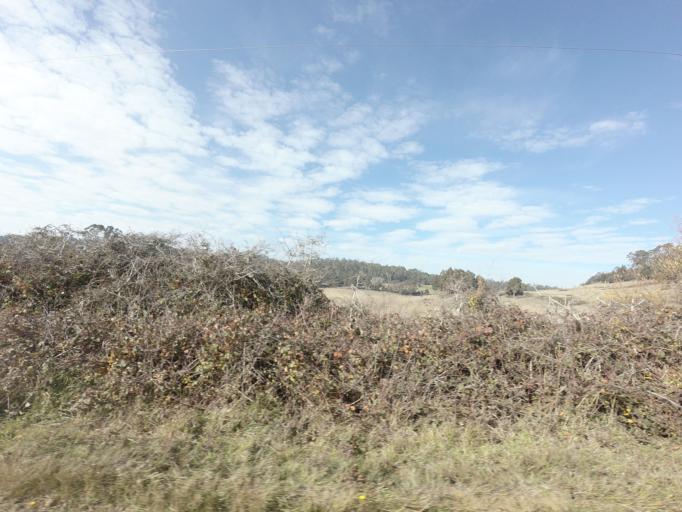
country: AU
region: Tasmania
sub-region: Sorell
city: Sorell
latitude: -42.4848
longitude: 147.4796
